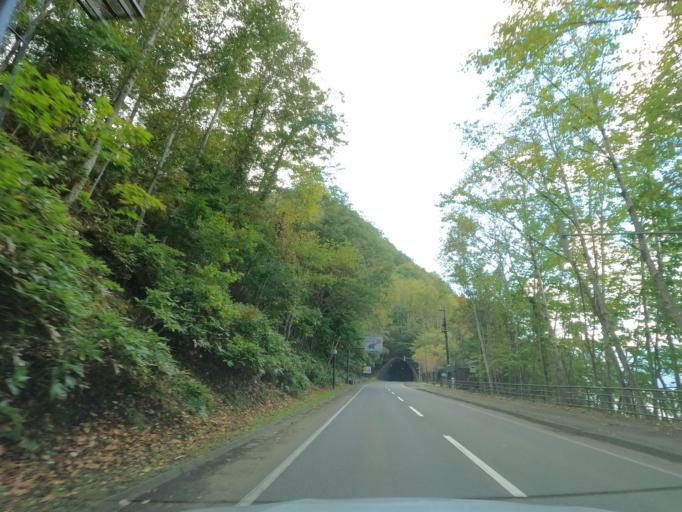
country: JP
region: Hokkaido
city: Shiraoi
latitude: 42.7047
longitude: 141.2926
